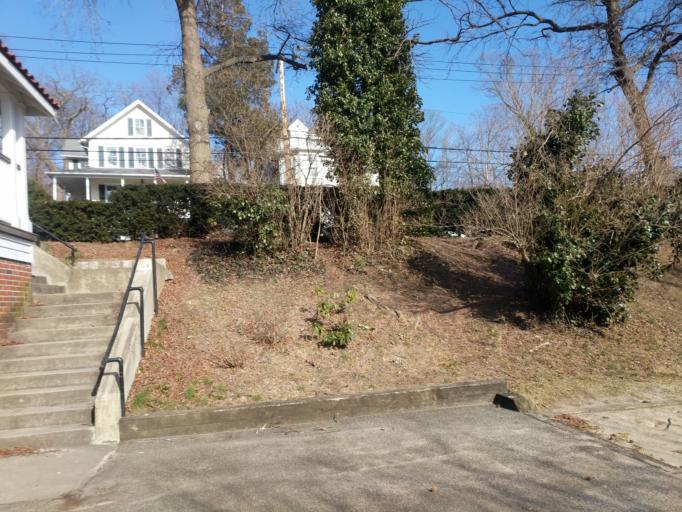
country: US
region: New York
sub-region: Suffolk County
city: Northport
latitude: 40.9010
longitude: -73.3521
